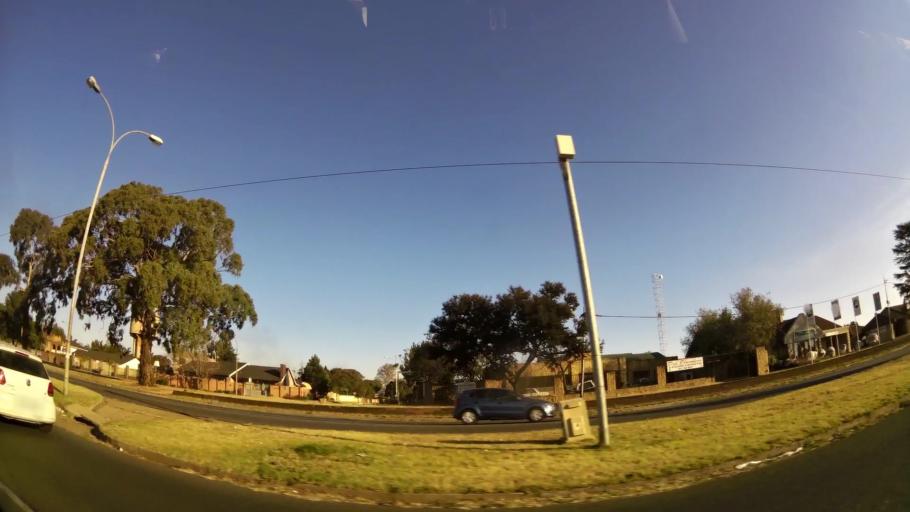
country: ZA
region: Gauteng
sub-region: City of Johannesburg Metropolitan Municipality
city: Roodepoort
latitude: -26.1465
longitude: 27.8852
